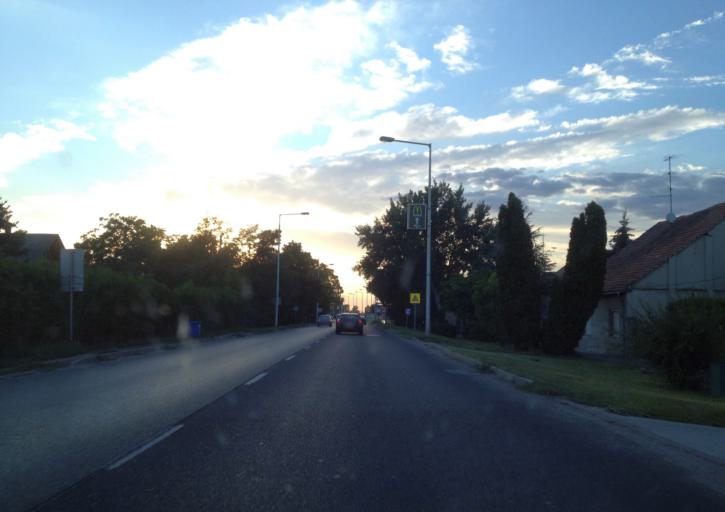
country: HU
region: Gyor-Moson-Sopron
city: Mosonmagyarovar
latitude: 47.8745
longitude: 17.2652
